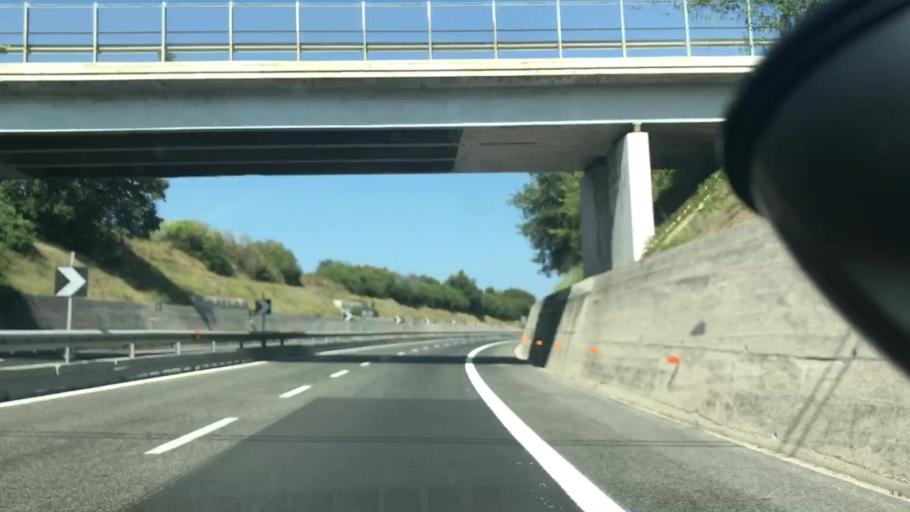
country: IT
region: Abruzzo
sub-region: Provincia di Chieti
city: San Vito Chietino
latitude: 42.3027
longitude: 14.4229
